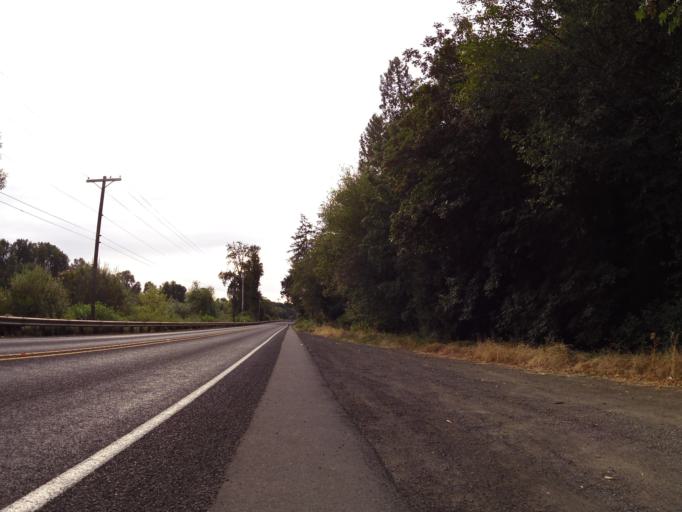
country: US
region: Washington
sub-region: Cowlitz County
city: West Longview
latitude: 46.1884
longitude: -123.0967
